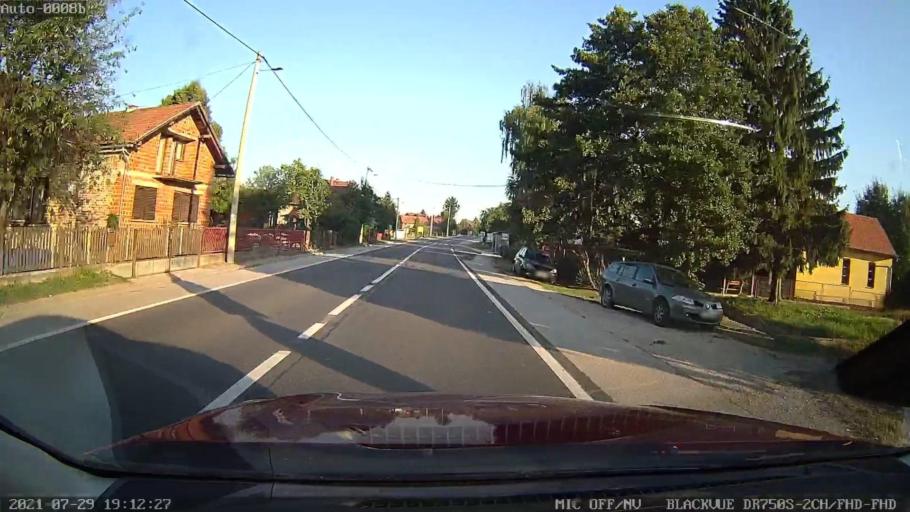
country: HR
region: Varazdinska
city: Jalzabet
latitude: 46.2674
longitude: 16.5164
